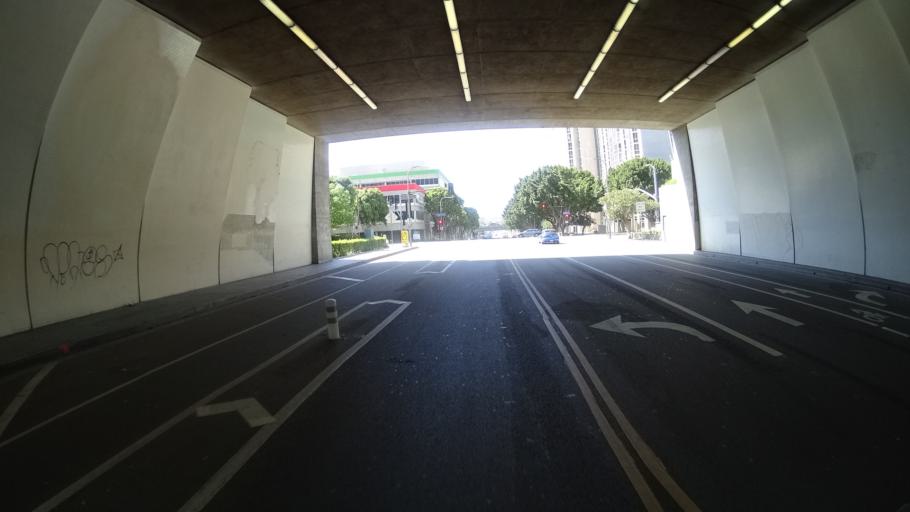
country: US
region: California
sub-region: Los Angeles County
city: Los Angeles
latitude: 34.0563
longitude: -118.2526
